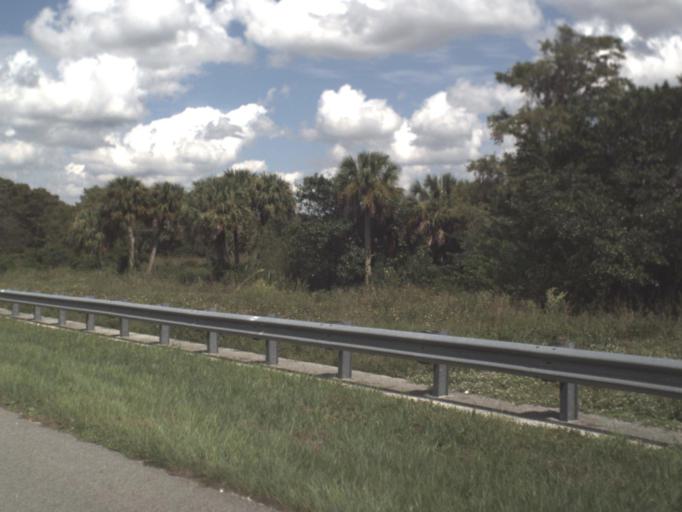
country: US
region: Florida
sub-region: Collier County
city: Immokalee
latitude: 26.3555
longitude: -81.3437
